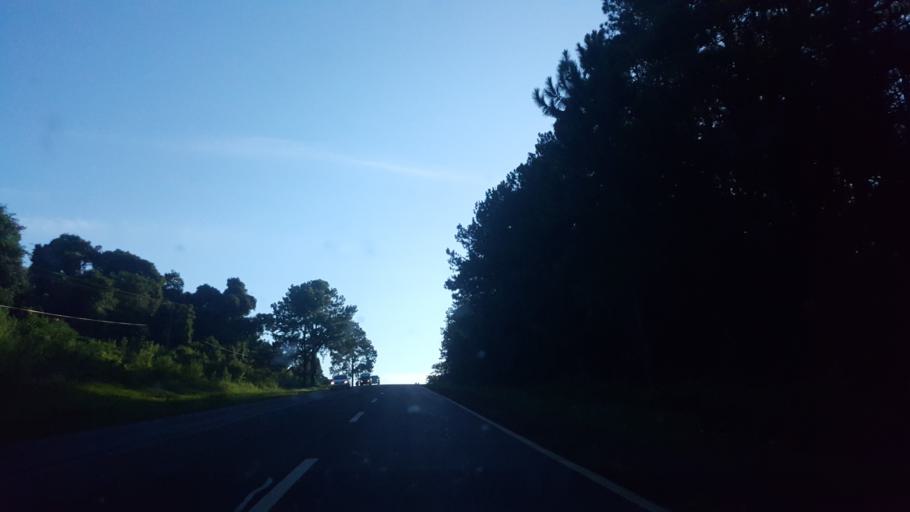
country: AR
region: Misiones
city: Caraguatay
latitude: -26.6669
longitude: -54.7628
